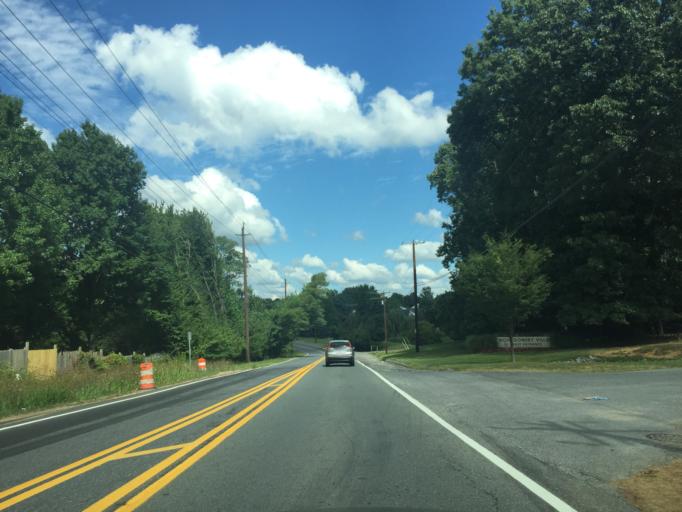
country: US
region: Maryland
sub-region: Montgomery County
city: Montgomery Village
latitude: 39.1796
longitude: -77.1797
